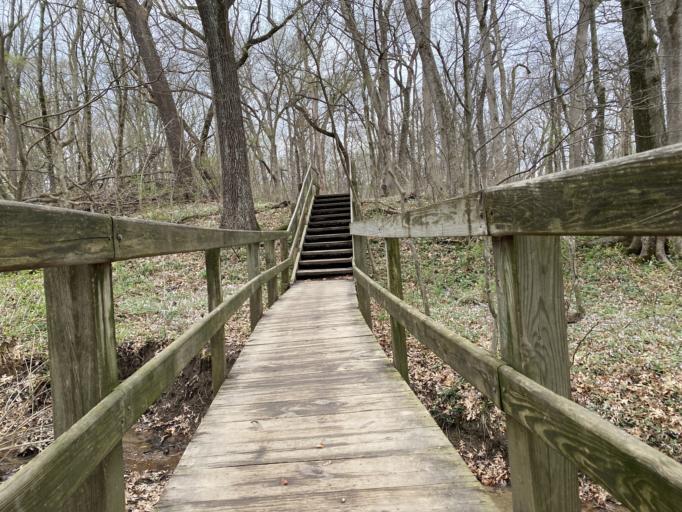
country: US
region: Illinois
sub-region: LaSalle County
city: Deer Park
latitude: 41.3166
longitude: -88.9877
